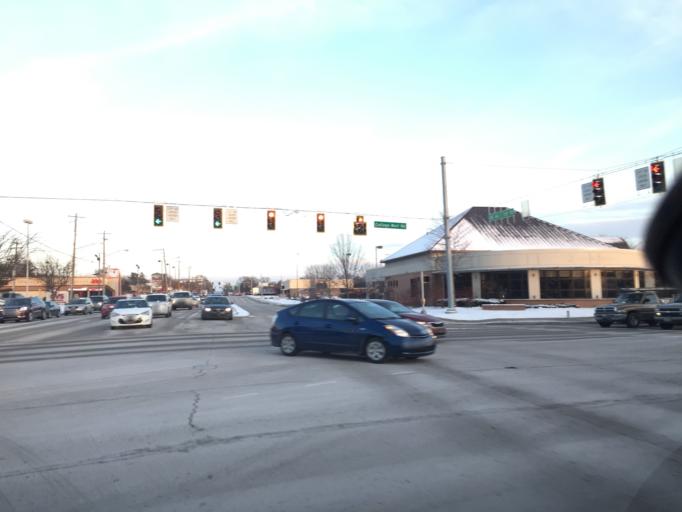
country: US
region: Indiana
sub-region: Monroe County
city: Bloomington
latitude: 39.1642
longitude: -86.4984
